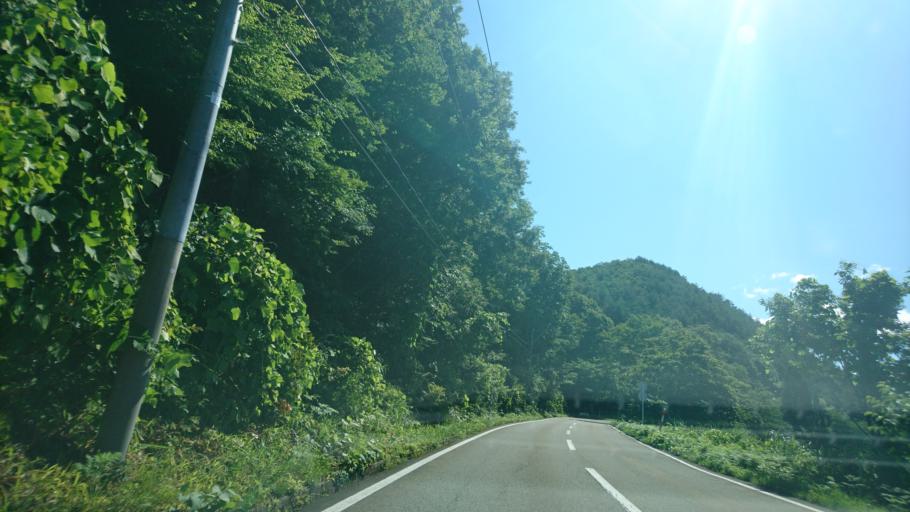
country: JP
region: Akita
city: Kakunodatemachi
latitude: 39.7499
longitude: 140.6634
